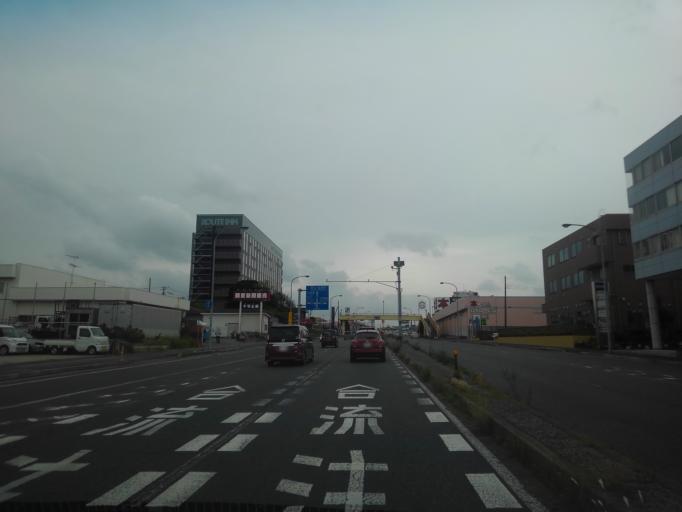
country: JP
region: Chiba
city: Kisarazu
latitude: 35.3832
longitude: 139.9421
